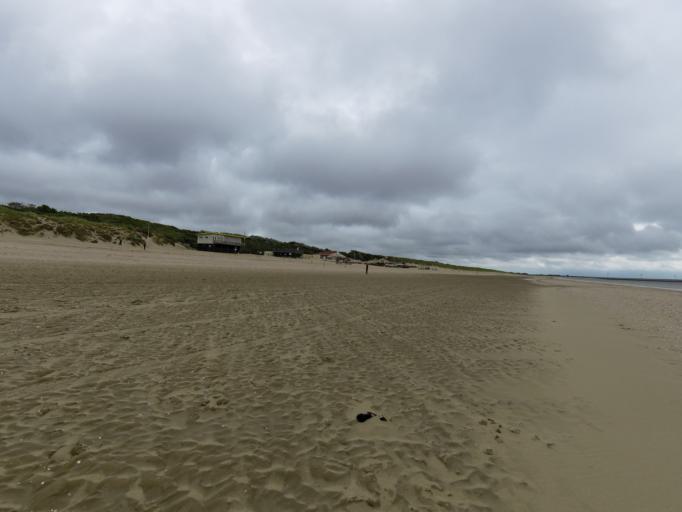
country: NL
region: South Holland
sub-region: Gemeente Goeree-Overflakkee
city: Goedereede
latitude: 51.8702
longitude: 4.0476
